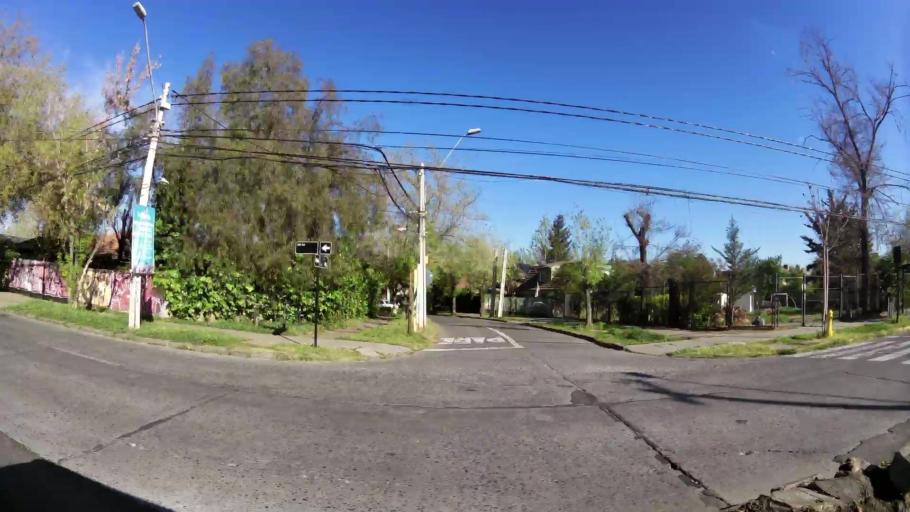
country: CL
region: Santiago Metropolitan
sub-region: Provincia de Santiago
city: Villa Presidente Frei, Nunoa, Santiago, Chile
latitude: -33.4524
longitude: -70.5514
